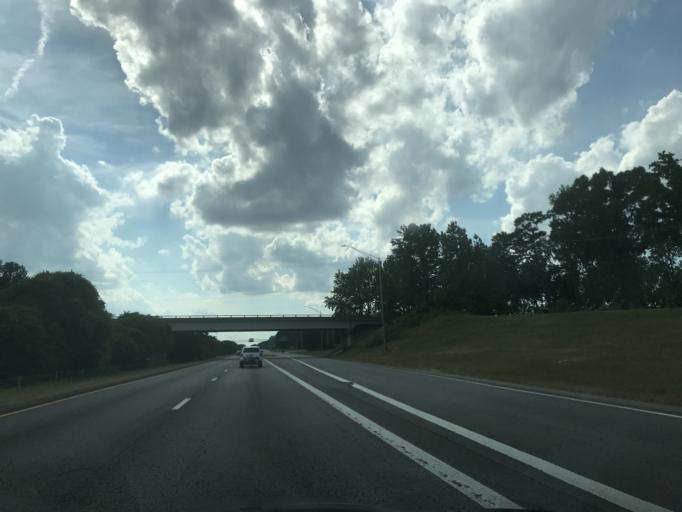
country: US
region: North Carolina
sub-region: Nash County
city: Red Oak
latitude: 35.9814
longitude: -77.8673
